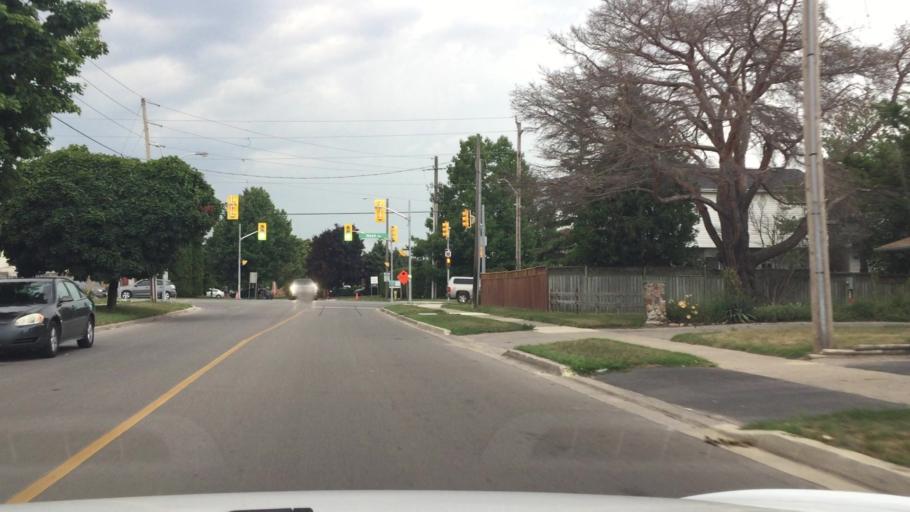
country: CA
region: Ontario
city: Oshawa
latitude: 43.9102
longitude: -78.8043
